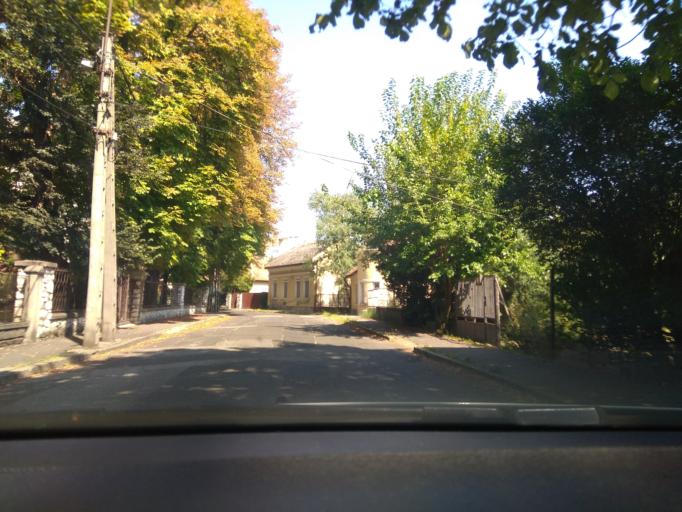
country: HU
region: Borsod-Abauj-Zemplen
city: Miskolc
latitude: 48.0721
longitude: 20.7858
